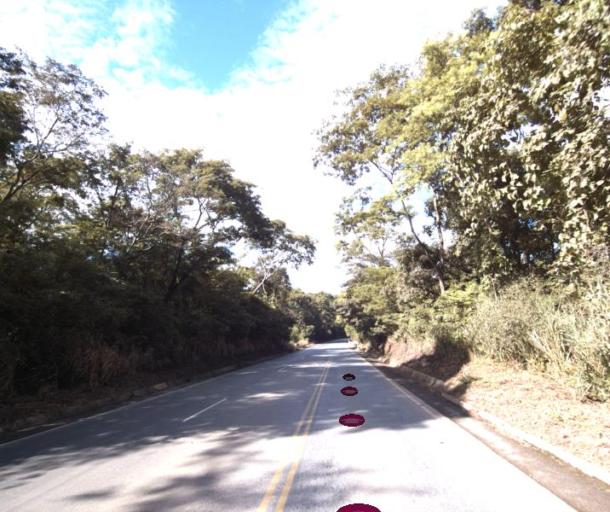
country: BR
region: Goias
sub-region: Uruacu
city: Uruacu
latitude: -14.7210
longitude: -49.2315
